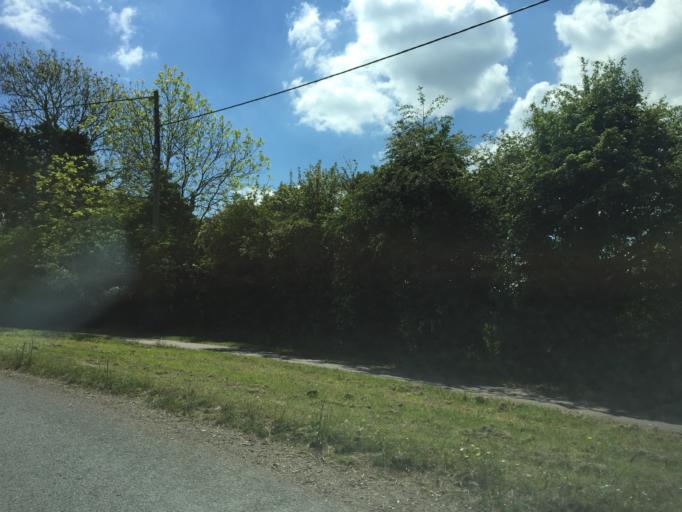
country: GB
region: England
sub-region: Milton Keynes
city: Wavendon
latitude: 52.0249
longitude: -0.6663
